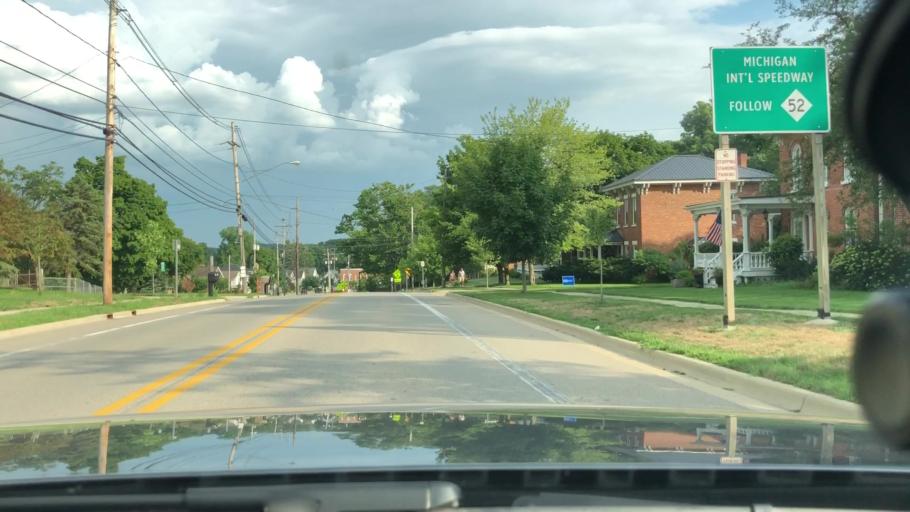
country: US
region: Michigan
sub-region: Washtenaw County
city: Manchester
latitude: 42.1523
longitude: -84.0400
